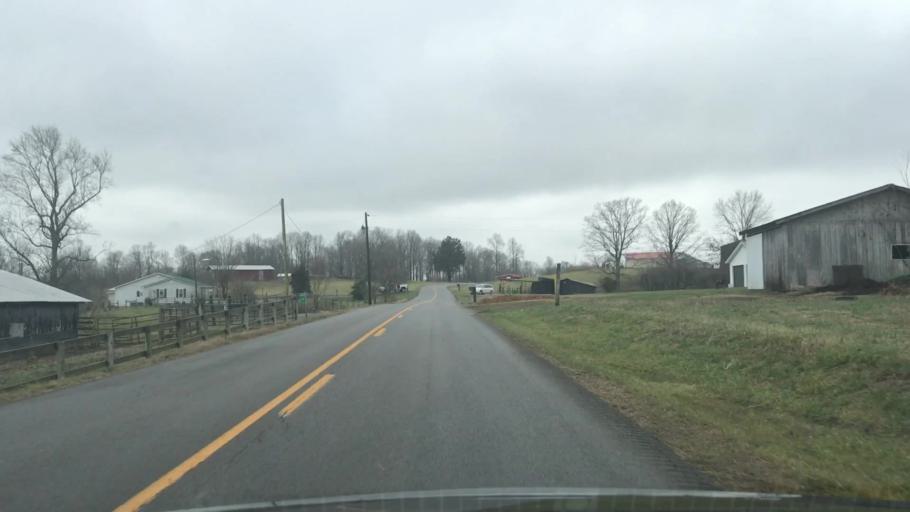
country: US
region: Kentucky
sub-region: Monroe County
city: Tompkinsville
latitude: 36.7867
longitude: -85.7389
